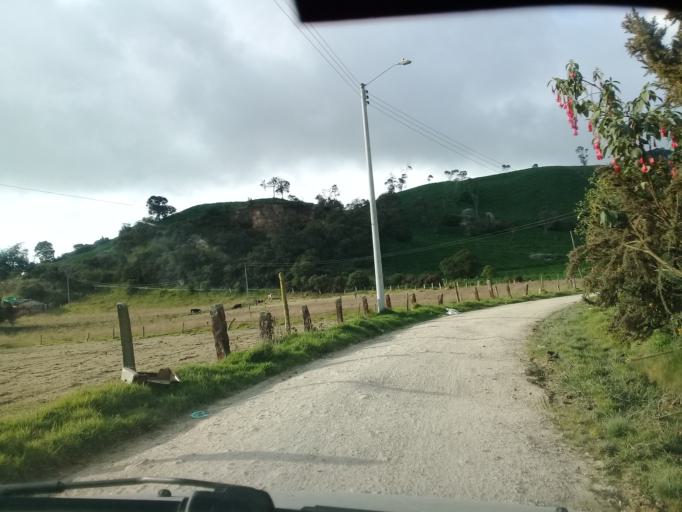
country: CO
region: Cundinamarca
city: Sibate
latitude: 4.4341
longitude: -74.2873
